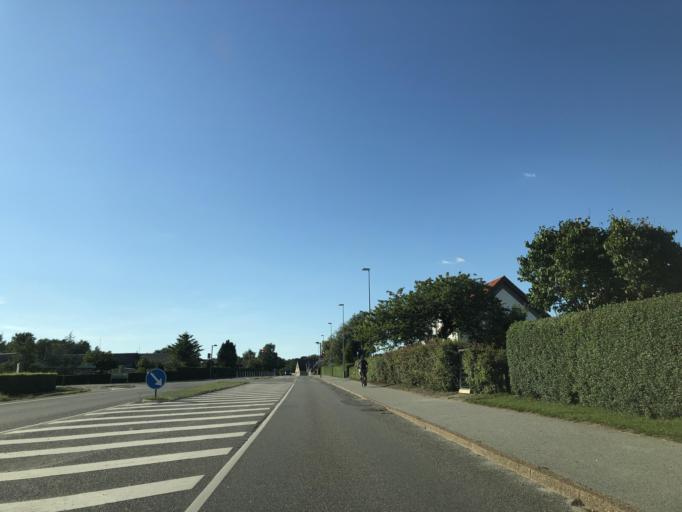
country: DK
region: North Denmark
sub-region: Mariagerfjord Kommune
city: Hobro
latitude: 56.6315
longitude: 9.8151
